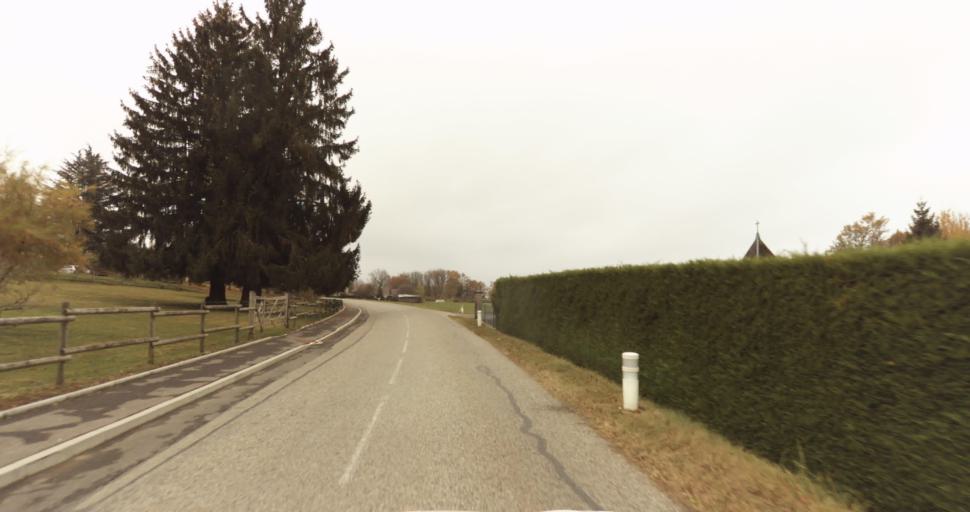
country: FR
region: Rhone-Alpes
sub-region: Departement de la Haute-Savoie
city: Saint-Felix
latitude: 45.7886
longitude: 5.9885
